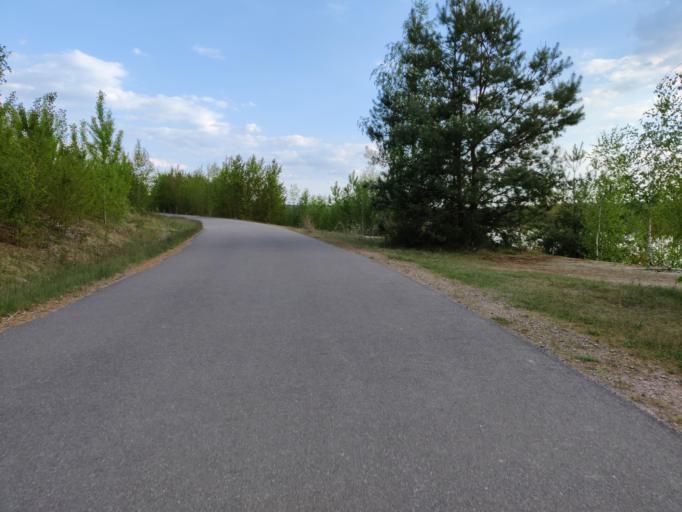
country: DE
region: Saxony
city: Rotha
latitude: 51.2276
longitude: 12.4365
